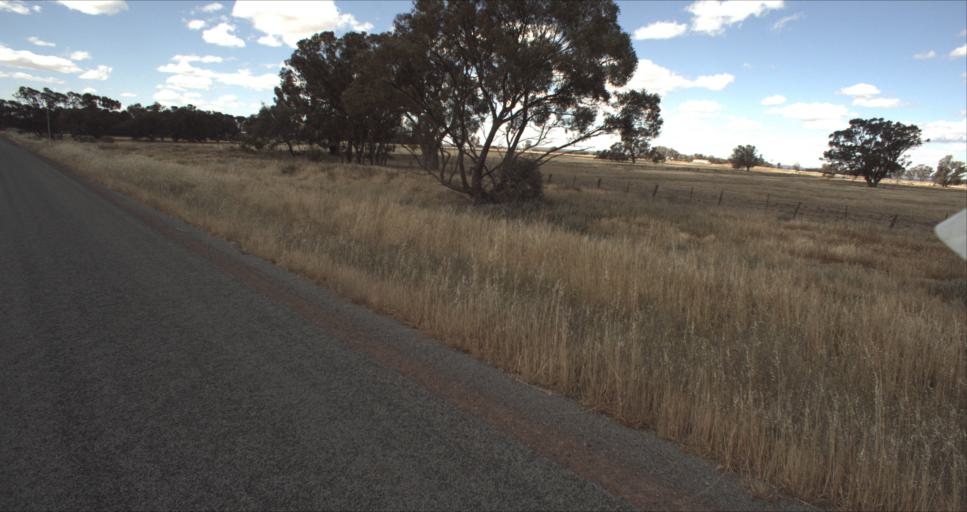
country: AU
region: New South Wales
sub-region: Leeton
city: Leeton
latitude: -34.4887
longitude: 146.2477
